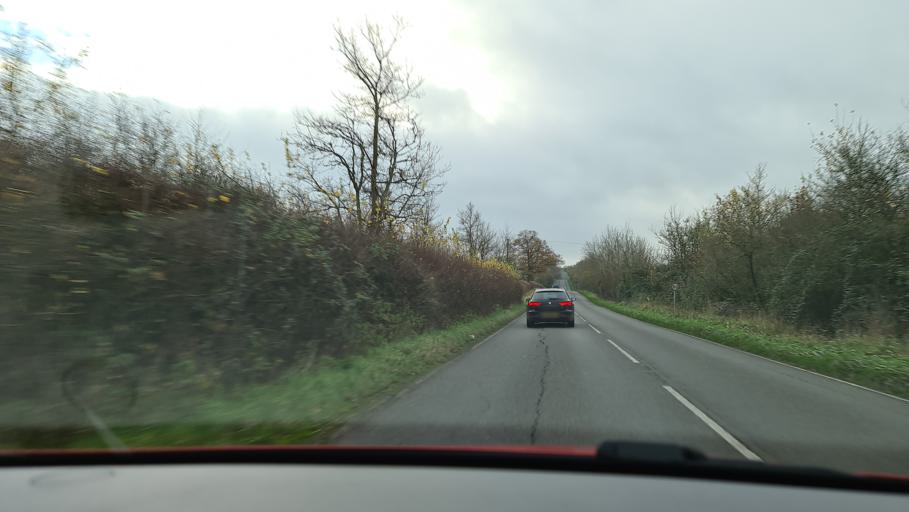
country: GB
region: England
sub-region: Oxfordshire
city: Bicester
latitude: 51.8455
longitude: -1.0883
